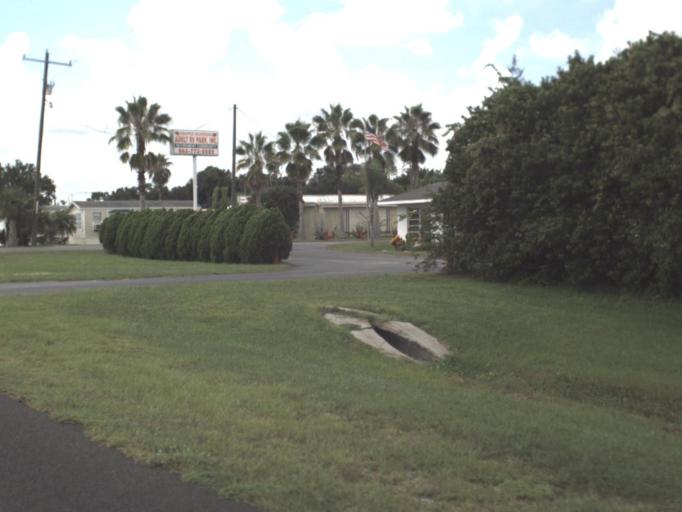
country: US
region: Florida
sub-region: Hardee County
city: Bowling Green
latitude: 27.6013
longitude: -81.8238
